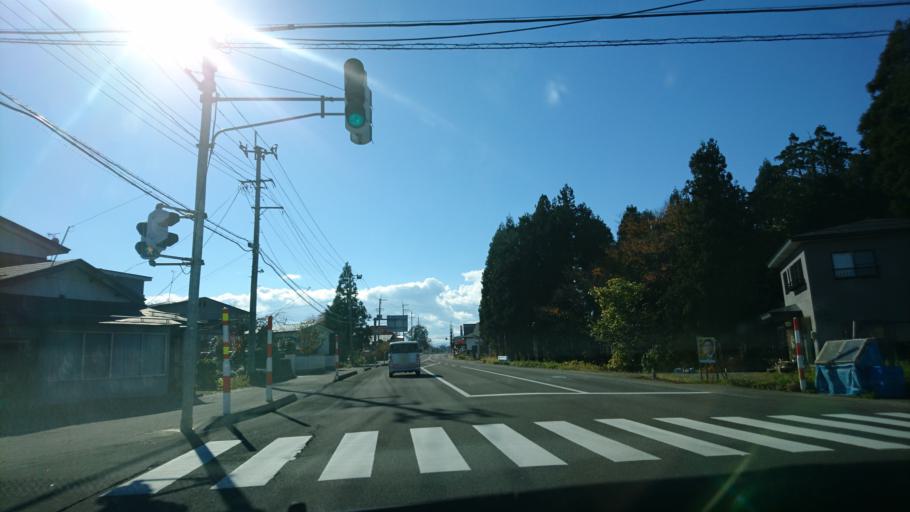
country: JP
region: Akita
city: Yokotemachi
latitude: 39.2742
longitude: 140.5019
